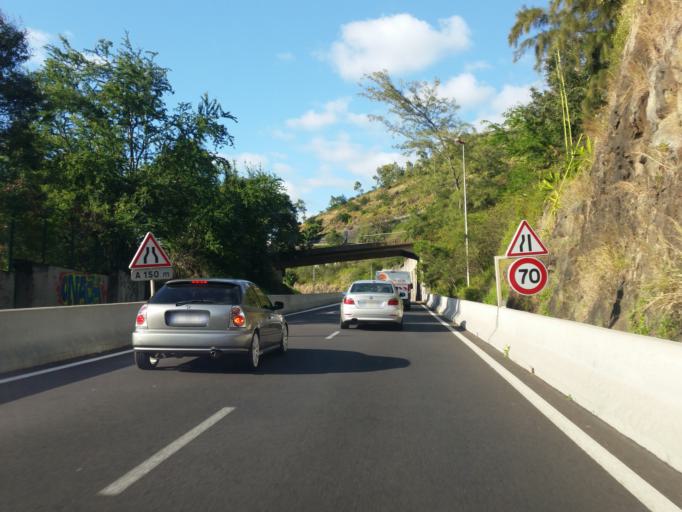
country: RE
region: Reunion
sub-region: Reunion
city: Saint-Denis
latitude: -20.8853
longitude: 55.4397
